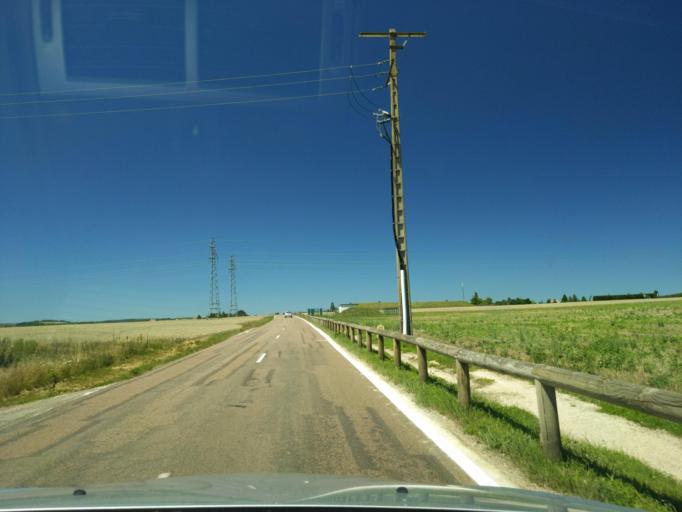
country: FR
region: Bourgogne
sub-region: Departement de la Cote-d'Or
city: Ruffey-les-Echirey
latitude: 47.3822
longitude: 5.0596
